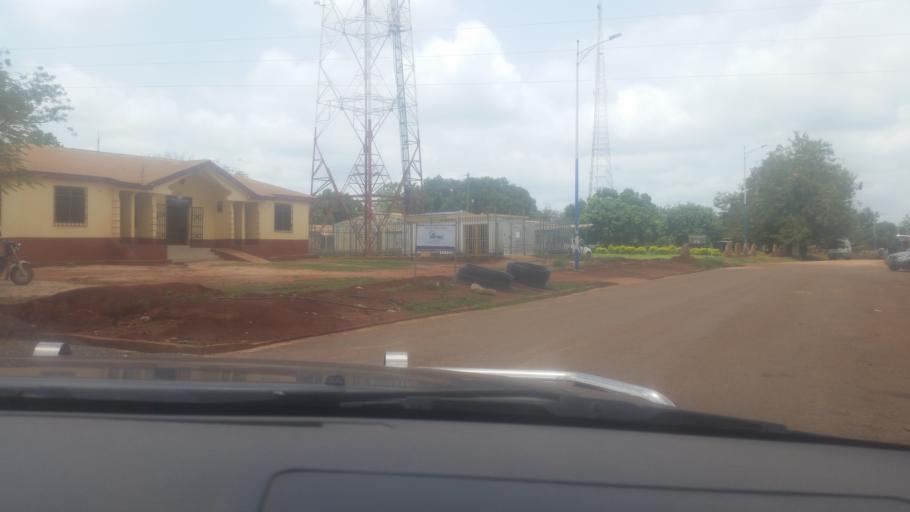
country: GH
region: Western
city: Bibiani
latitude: 6.8066
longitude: -2.5184
